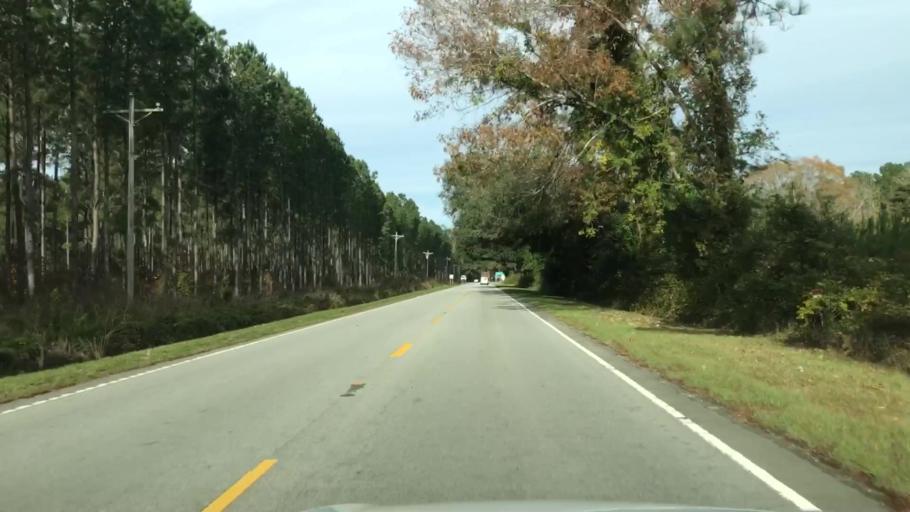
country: US
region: South Carolina
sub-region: Colleton County
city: Walterboro
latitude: 32.7935
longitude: -80.4850
